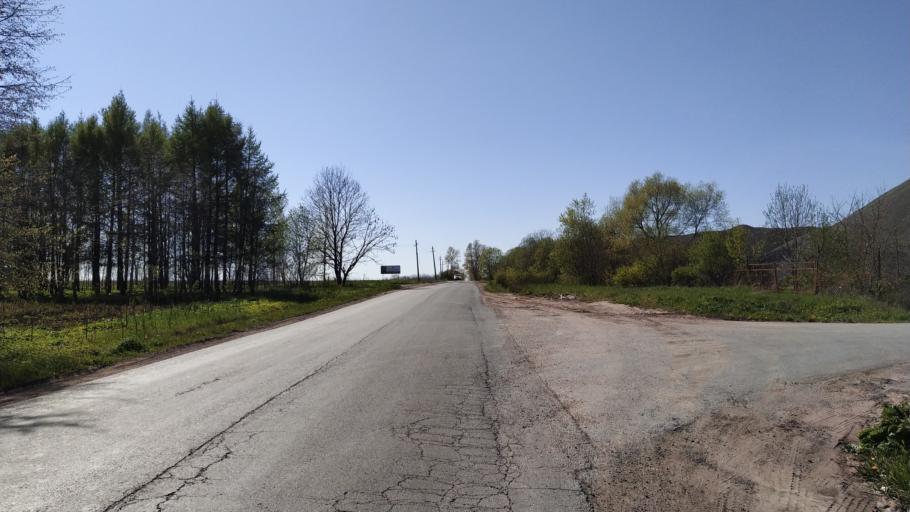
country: RU
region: St.-Petersburg
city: Pushkin
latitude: 59.6849
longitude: 30.3843
